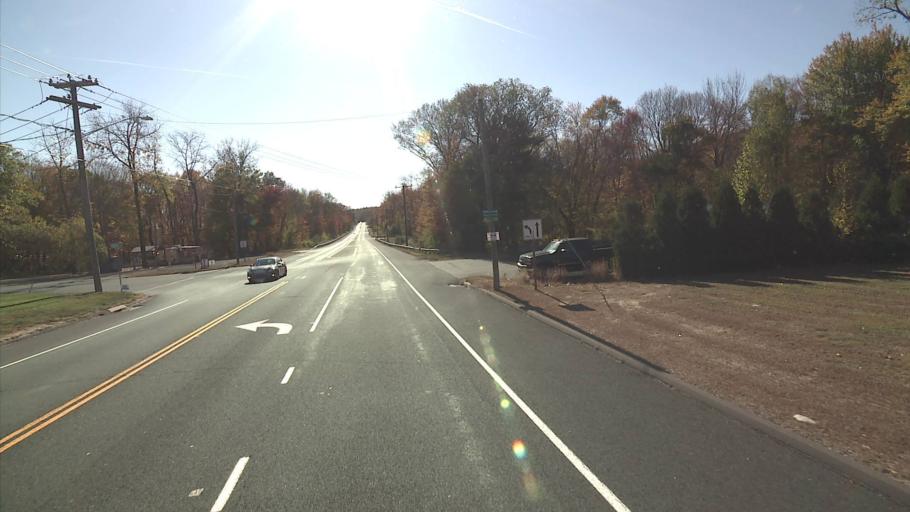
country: US
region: Connecticut
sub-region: Tolland County
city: Coventry Lake
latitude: 41.7572
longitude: -72.4010
